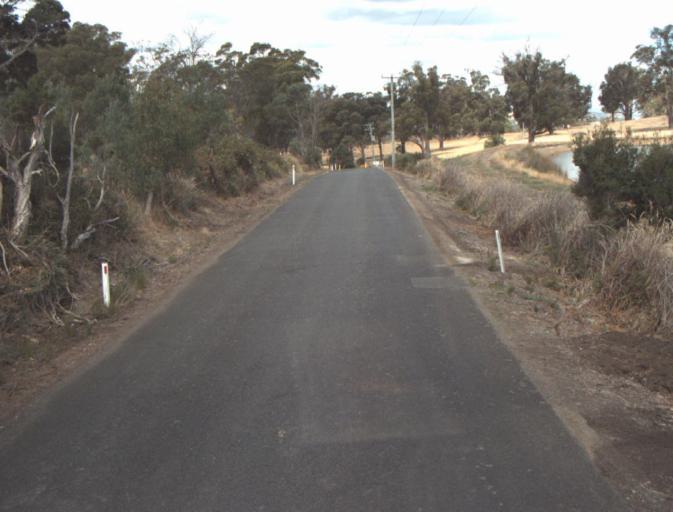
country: AU
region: Tasmania
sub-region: Launceston
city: Mayfield
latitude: -41.3044
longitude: 147.0381
